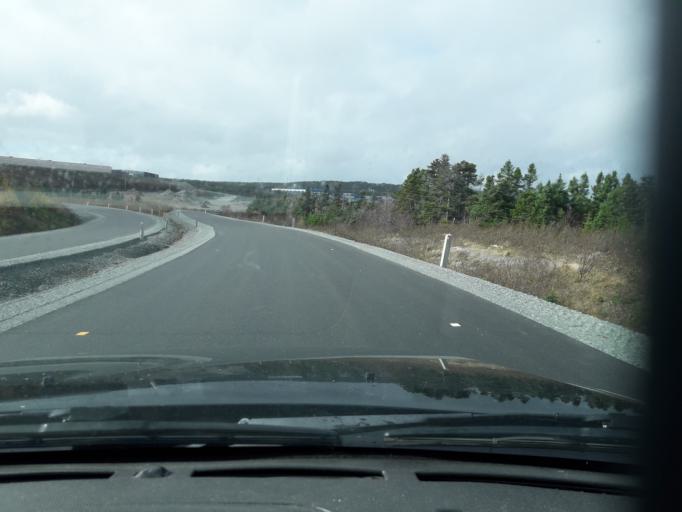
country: CA
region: Newfoundland and Labrador
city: Mount Pearl
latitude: 47.5559
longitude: -52.7731
